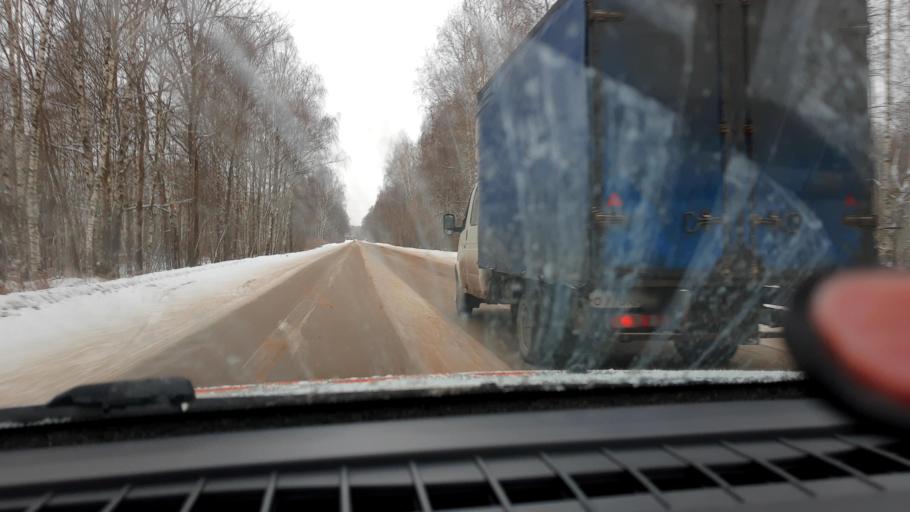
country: RU
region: Nizjnij Novgorod
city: Afonino
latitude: 56.3180
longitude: 44.1877
